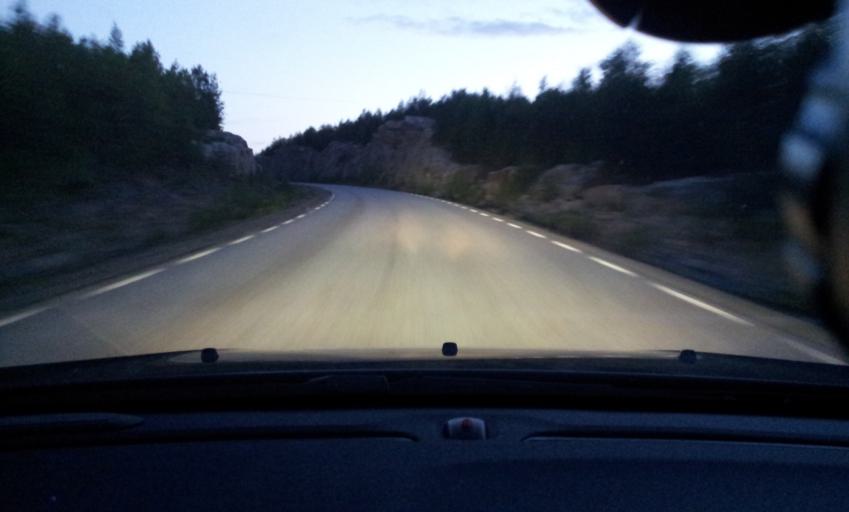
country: SE
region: Jaemtland
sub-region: Bergs Kommun
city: Hoverberg
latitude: 62.6764
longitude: 14.7092
